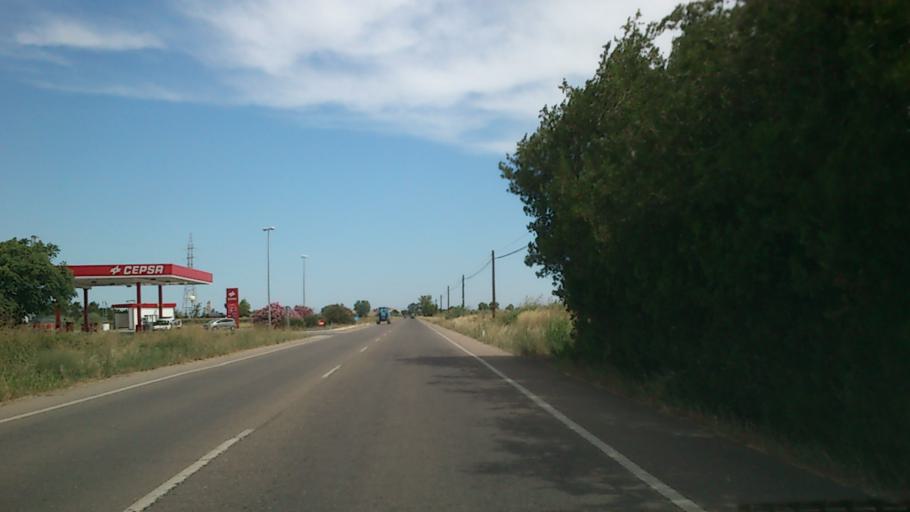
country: ES
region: Aragon
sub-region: Provincia de Zaragoza
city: Villanueva de Gallego
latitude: 41.7499
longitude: -0.8015
